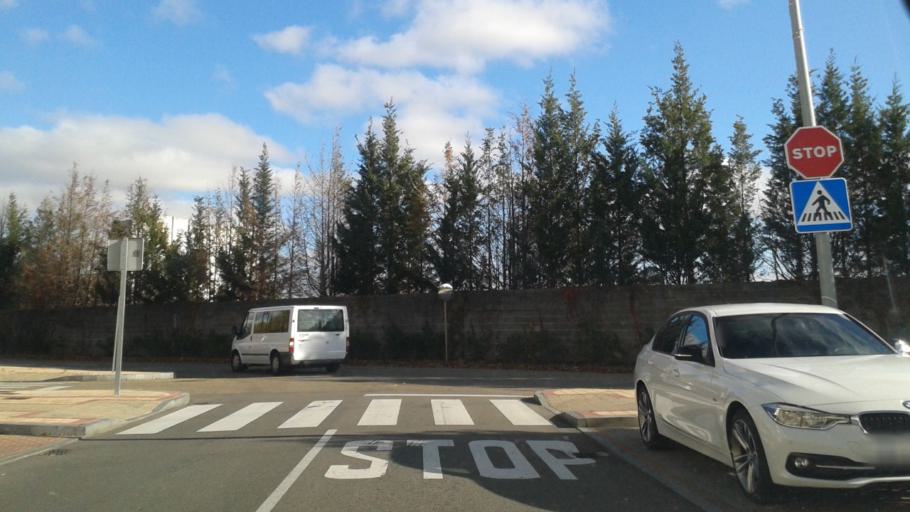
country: ES
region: Castille and Leon
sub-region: Provincia de Valladolid
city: Arroyo
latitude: 41.6189
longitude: -4.7750
